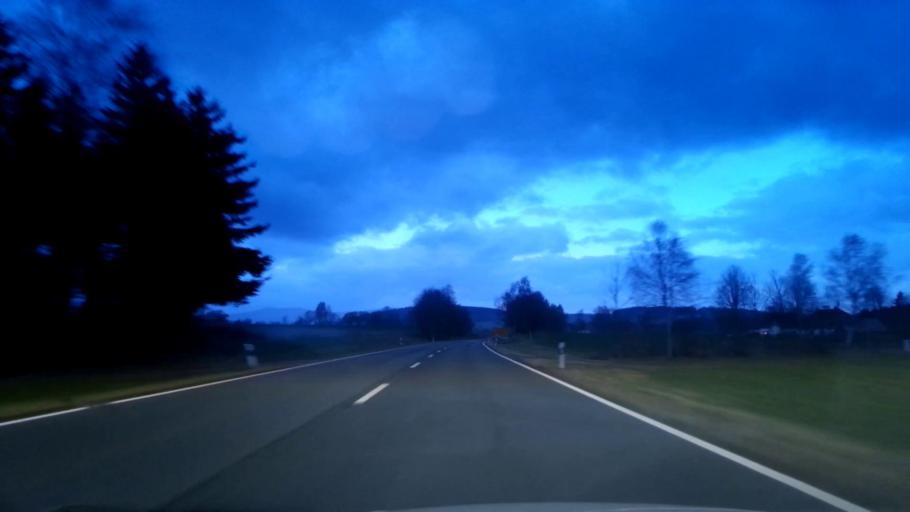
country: DE
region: Bavaria
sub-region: Upper Palatinate
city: Fuchsmuhl
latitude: 49.9492
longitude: 12.1029
